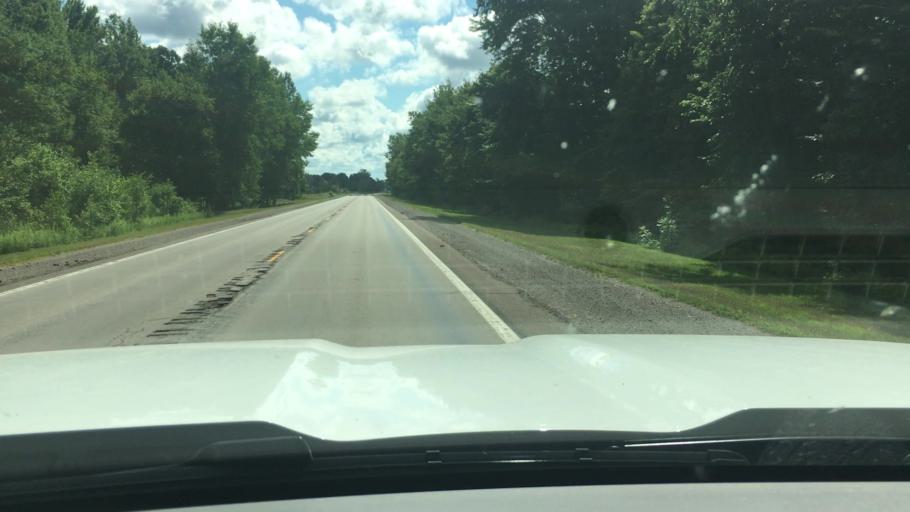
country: US
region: Michigan
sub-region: Shiawassee County
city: New Haven
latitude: 43.1867
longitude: -84.3124
